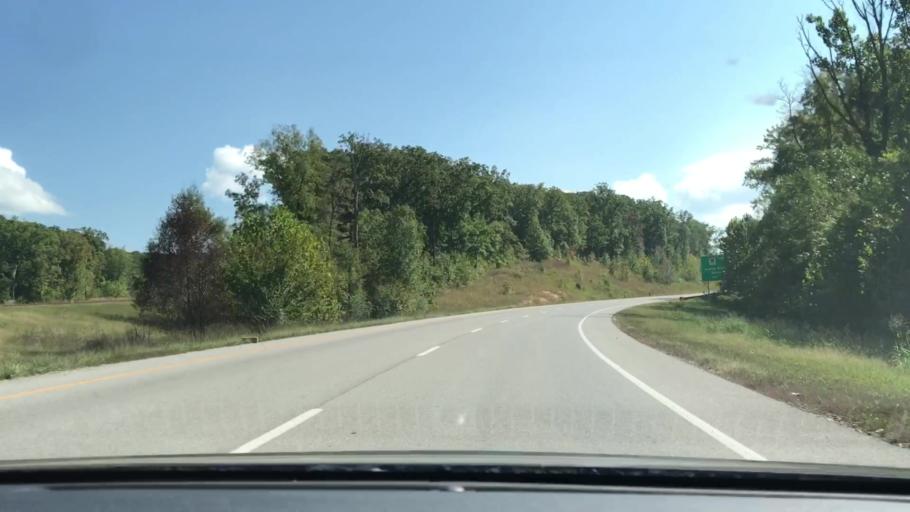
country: US
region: Kentucky
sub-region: Trigg County
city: Cadiz
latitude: 36.7791
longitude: -88.0912
